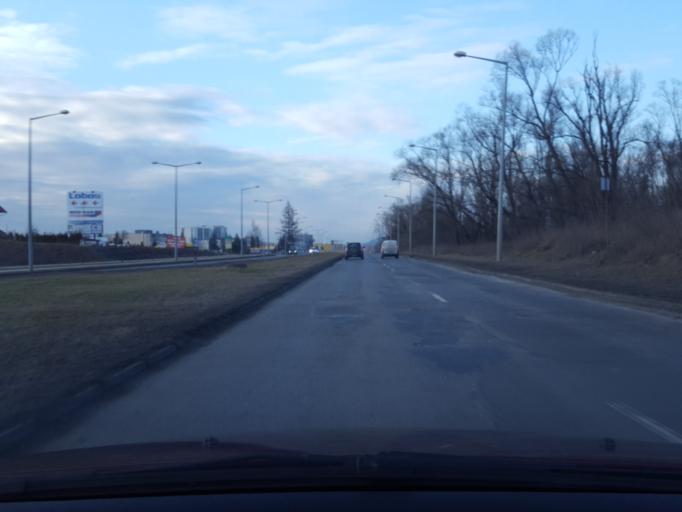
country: PL
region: Lesser Poland Voivodeship
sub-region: Powiat nowosadecki
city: Nawojowa
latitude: 49.5954
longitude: 20.7322
